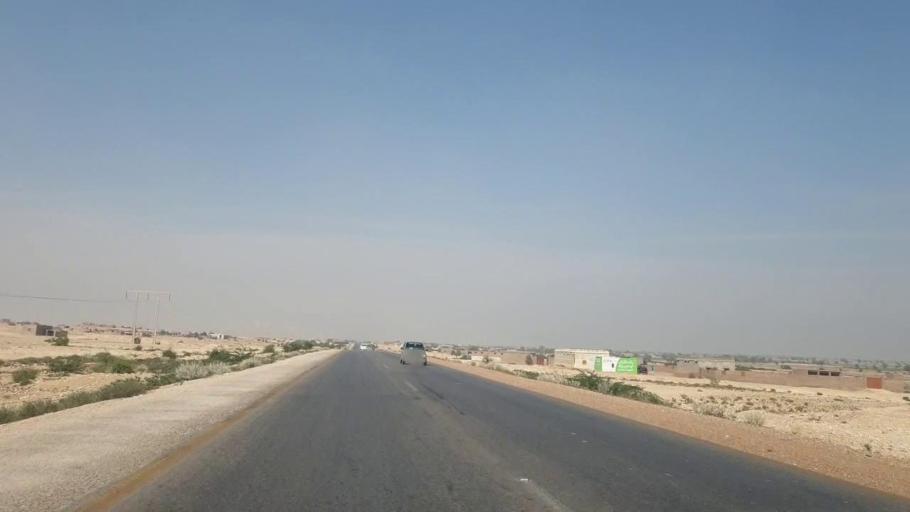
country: PK
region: Sindh
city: Hala
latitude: 25.7815
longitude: 68.2835
